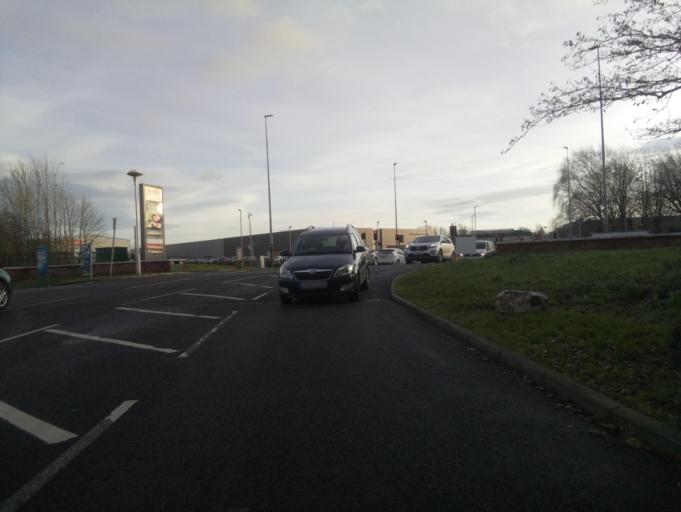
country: GB
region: England
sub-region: Cumbria
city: Scotby
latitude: 54.8961
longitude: -2.8959
